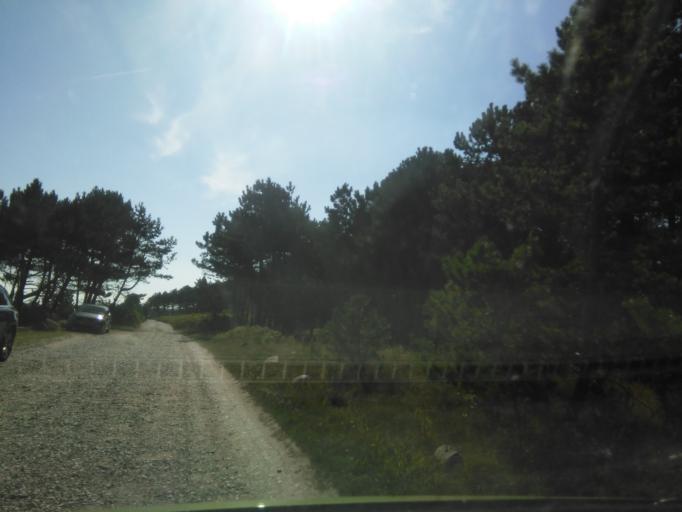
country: DK
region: Central Jutland
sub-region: Syddjurs Kommune
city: Ebeltoft
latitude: 56.2074
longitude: 10.7336
